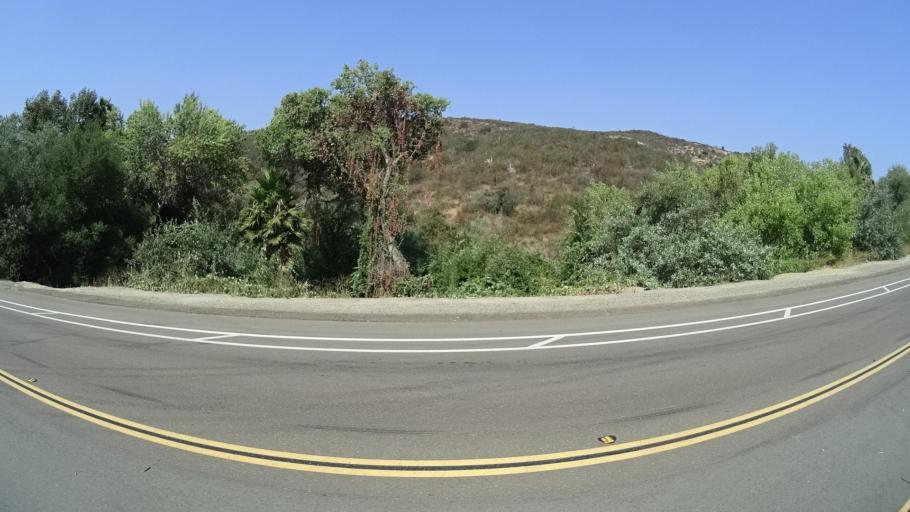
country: US
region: California
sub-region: San Diego County
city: Hidden Meadows
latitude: 33.2815
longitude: -117.1481
